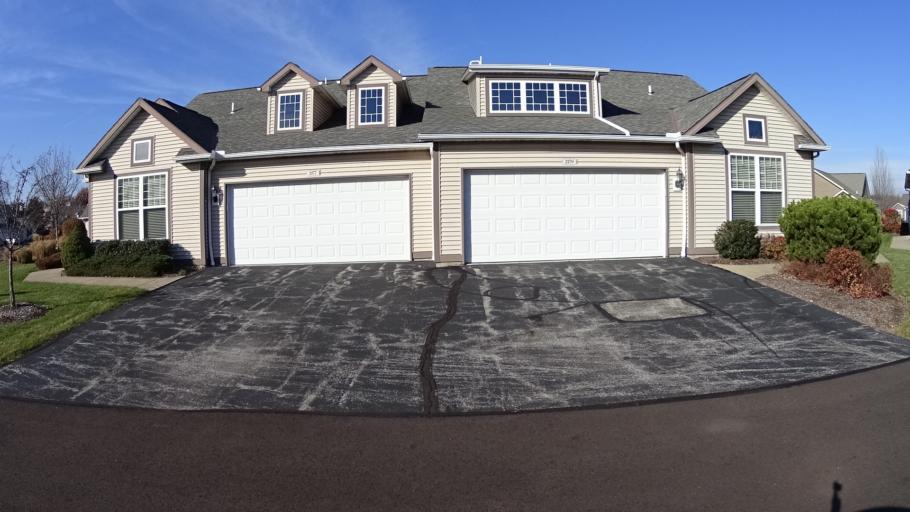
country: US
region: Ohio
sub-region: Lorain County
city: Avon Center
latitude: 41.4580
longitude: -82.0069
